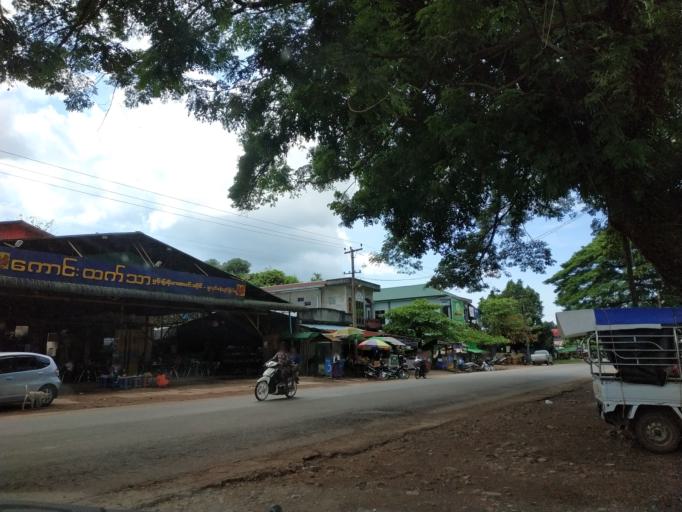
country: MM
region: Mon
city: Kyaikkami
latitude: 15.9510
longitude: 97.7308
